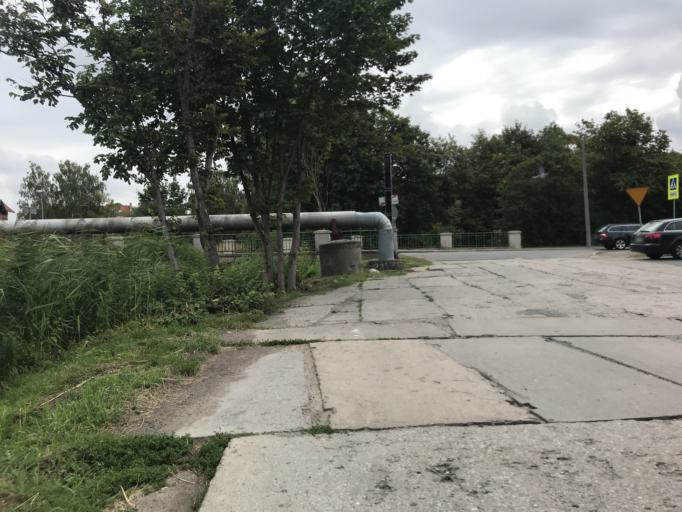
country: PL
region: Warmian-Masurian Voivodeship
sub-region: Powiat elblaski
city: Elblag
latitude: 54.1552
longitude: 19.3905
